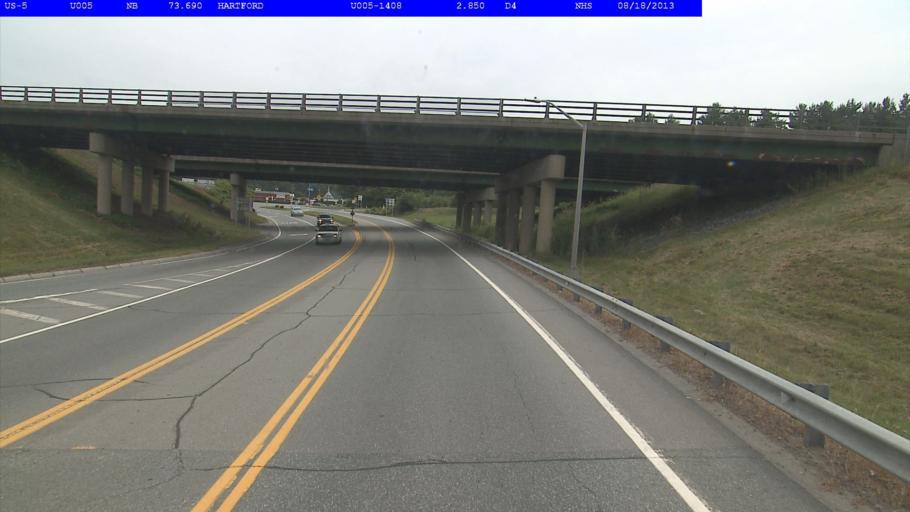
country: US
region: Vermont
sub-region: Windsor County
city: White River Junction
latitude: 43.6454
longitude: -72.3387
